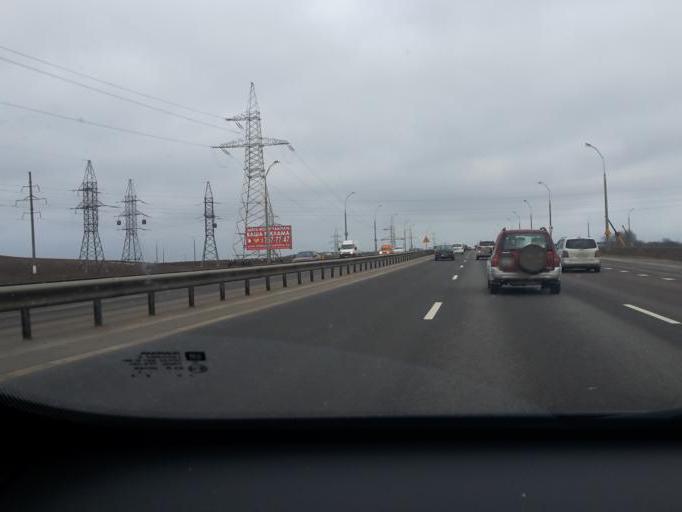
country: BY
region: Minsk
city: Novoye Medvezhino
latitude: 53.8915
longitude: 27.4121
